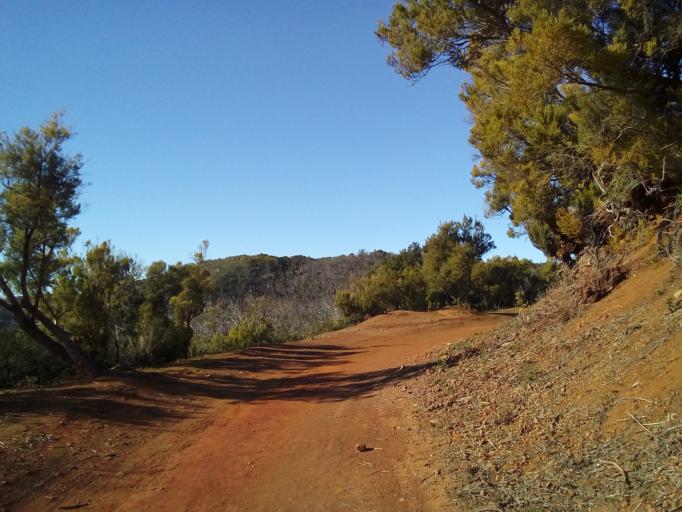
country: ES
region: Canary Islands
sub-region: Provincia de Santa Cruz de Tenerife
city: Vallehermosa
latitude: 28.1210
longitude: -17.2539
